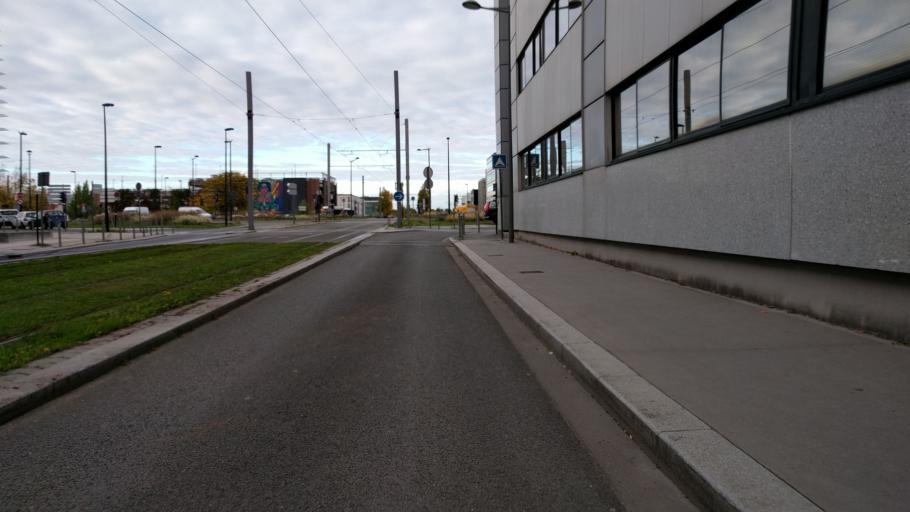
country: FR
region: Aquitaine
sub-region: Departement de la Gironde
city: Le Bouscat
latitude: 44.8650
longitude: -0.5756
